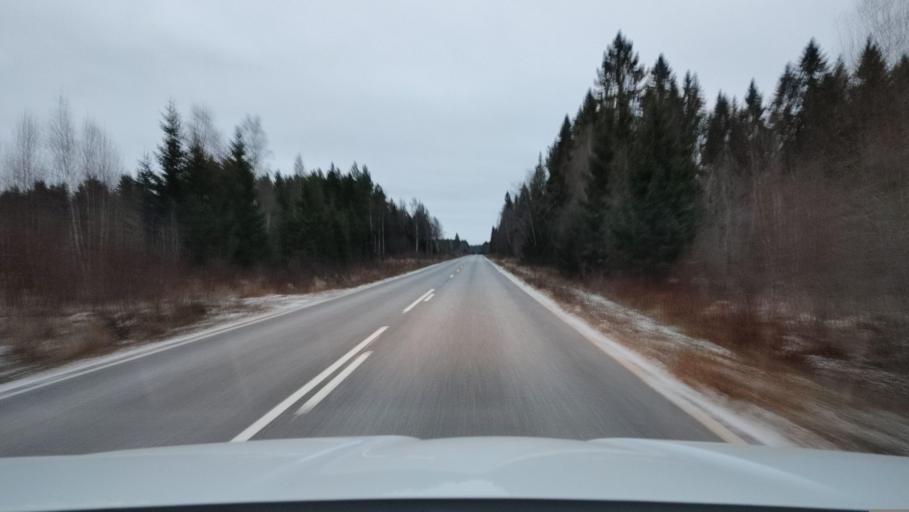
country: FI
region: Ostrobothnia
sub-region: Vaasa
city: Replot
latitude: 63.2474
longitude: 21.3778
